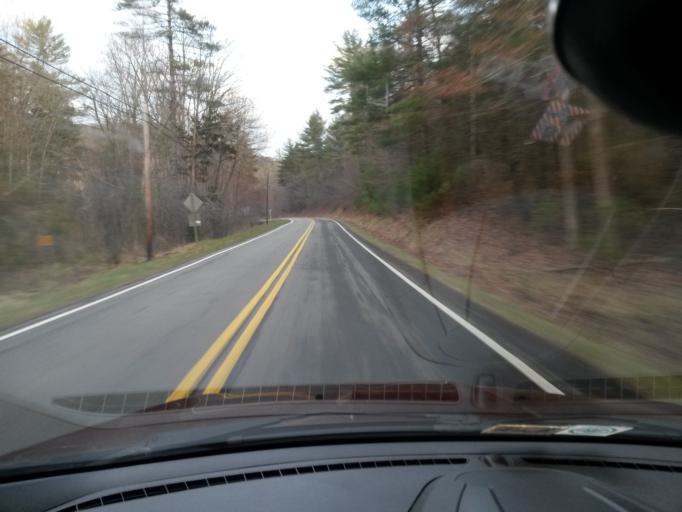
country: US
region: Virginia
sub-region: City of Covington
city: Covington
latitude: 37.8057
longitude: -80.0720
